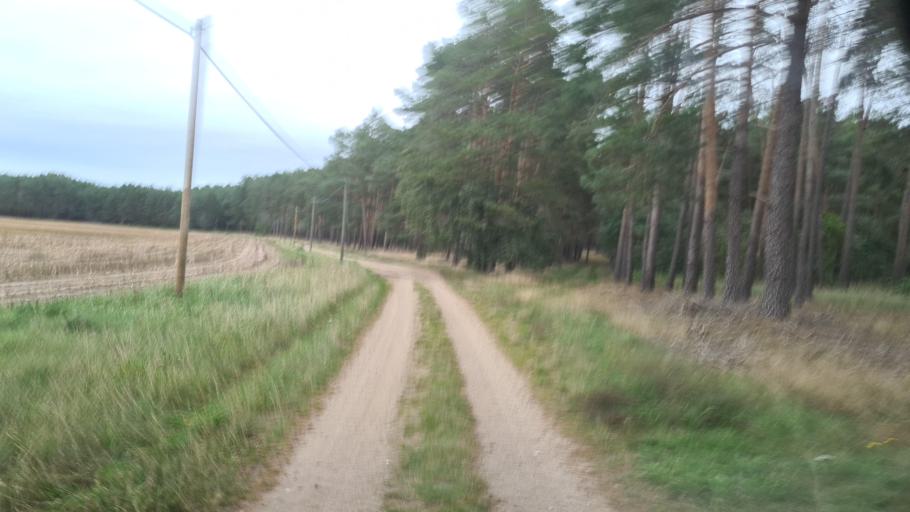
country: DE
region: Brandenburg
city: Drahnsdorf
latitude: 51.9512
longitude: 13.5697
